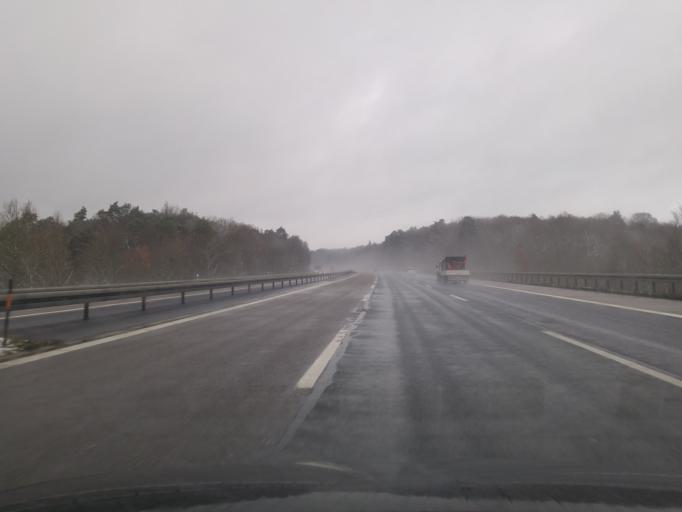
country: DE
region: Bavaria
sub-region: Regierungsbezirk Unterfranken
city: Elfershausen
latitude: 50.1606
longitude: 9.9636
